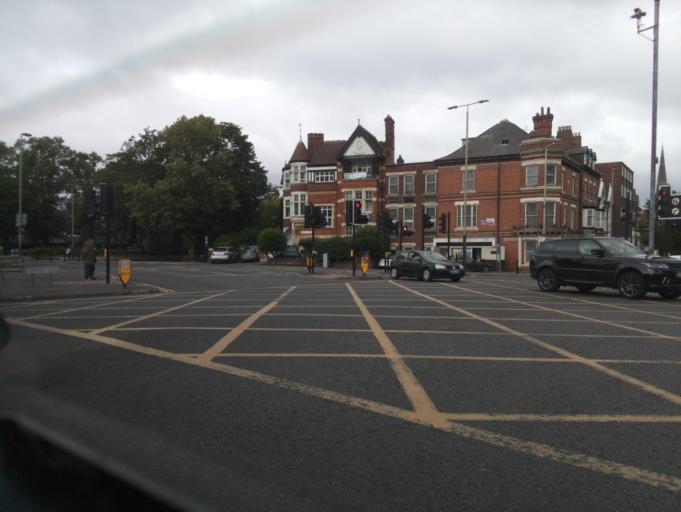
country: GB
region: England
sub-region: City of Leicester
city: Leicester
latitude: 52.6266
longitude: -1.1185
